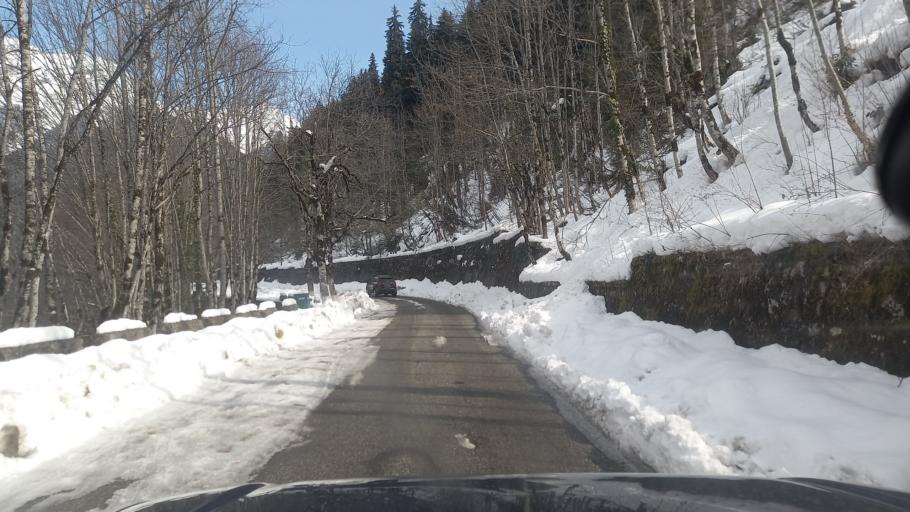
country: GE
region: Abkhazia
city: Gagra
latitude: 43.4718
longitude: 40.5349
